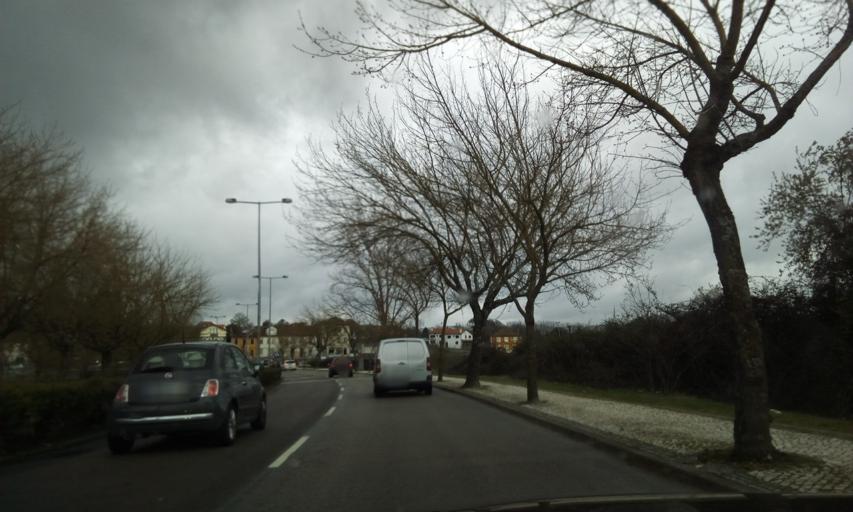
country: PT
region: Viseu
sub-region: Viseu
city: Viseu
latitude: 40.6639
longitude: -7.9060
